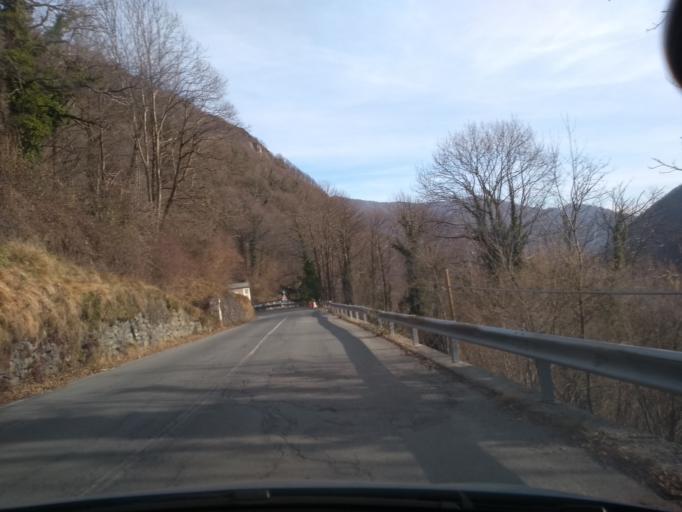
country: IT
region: Piedmont
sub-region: Provincia di Torino
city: Ceres
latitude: 45.3207
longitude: 7.3568
